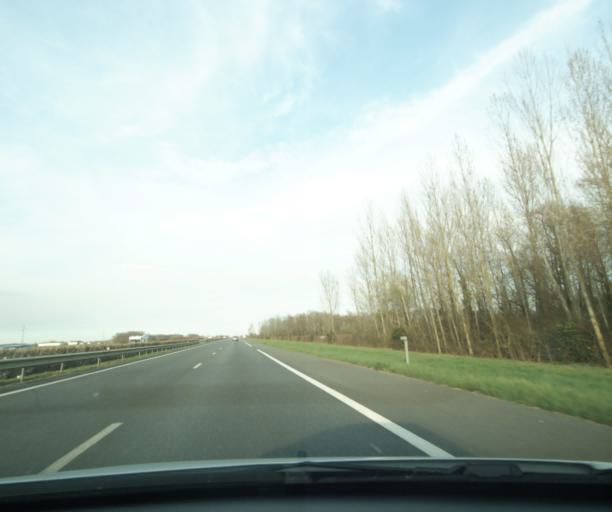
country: FR
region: Midi-Pyrenees
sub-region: Departement de la Haute-Garonne
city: Cazeres
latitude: 43.2458
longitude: 1.0906
